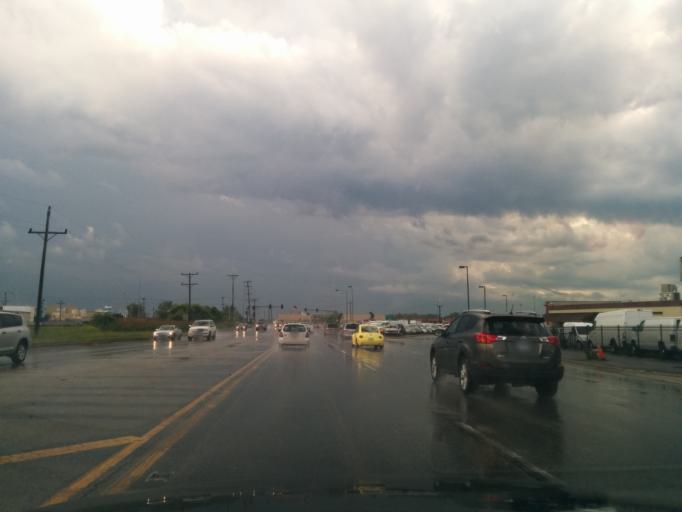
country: US
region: Illinois
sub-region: Cook County
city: Summit
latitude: 41.7759
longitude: -87.8013
